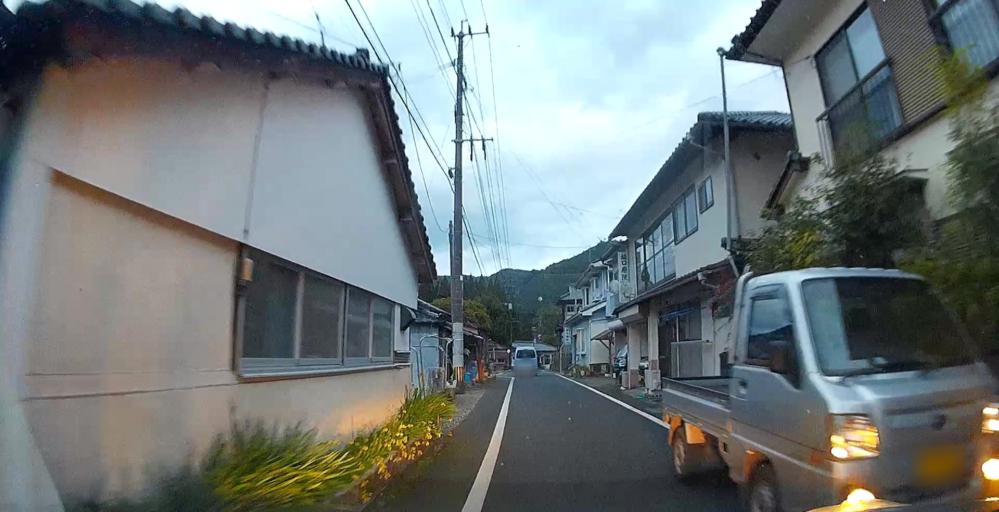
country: JP
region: Kumamoto
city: Minamata
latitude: 32.1516
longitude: 130.4414
